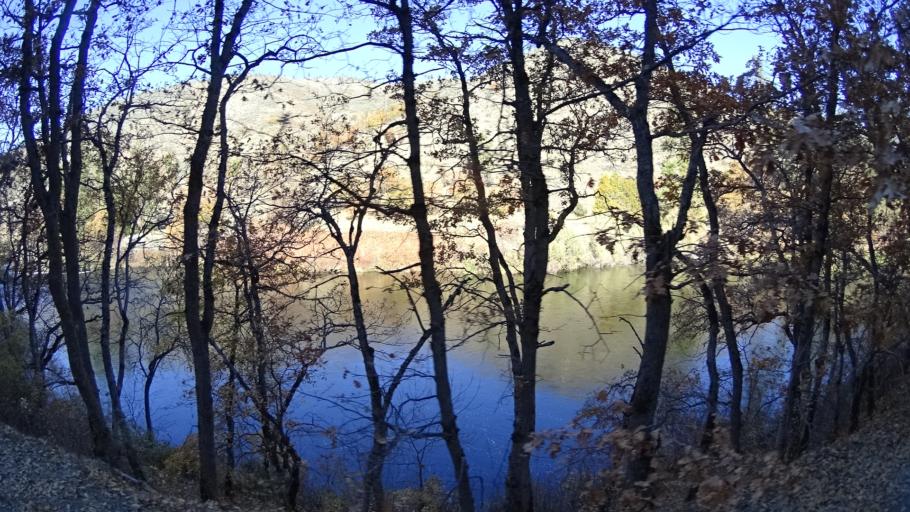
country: US
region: California
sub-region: Siskiyou County
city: Yreka
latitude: 41.8559
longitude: -122.7572
